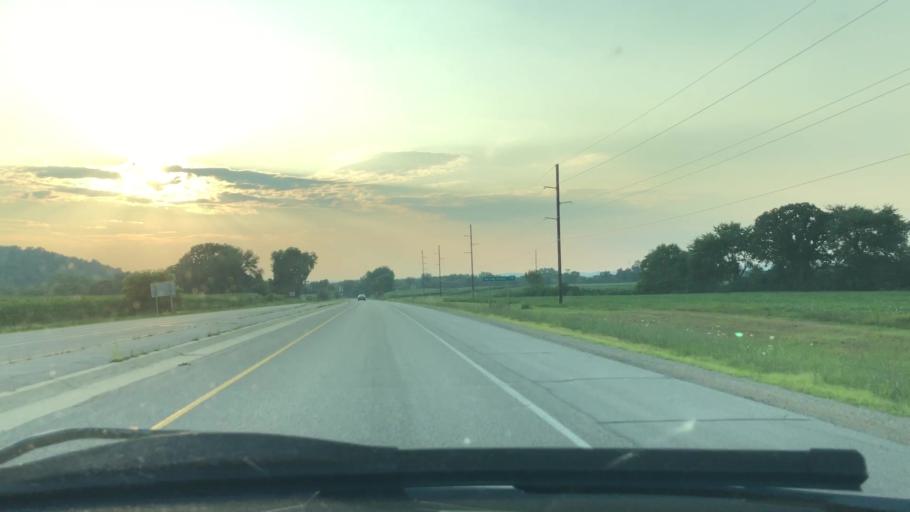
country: US
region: Wisconsin
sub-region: Dane County
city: Mazomanie
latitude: 43.1684
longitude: -89.7750
